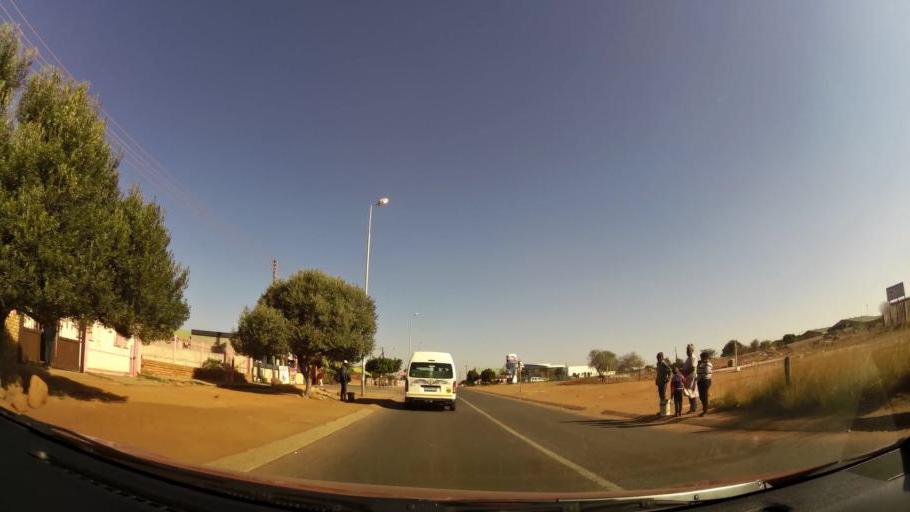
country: ZA
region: Gauteng
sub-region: City of Tshwane Metropolitan Municipality
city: Mabopane
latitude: -25.5395
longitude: 28.1054
